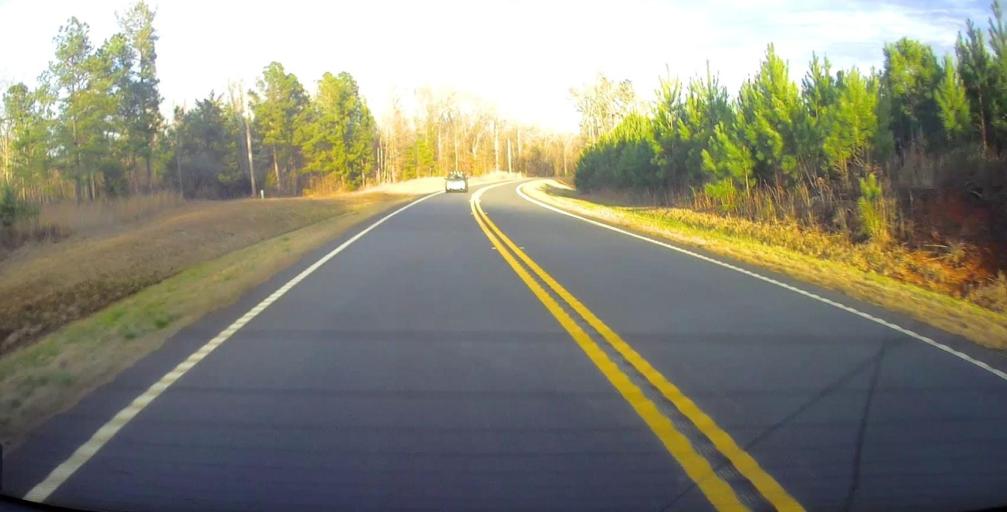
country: US
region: Georgia
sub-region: Talbot County
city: Sardis
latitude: 32.7213
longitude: -84.6581
